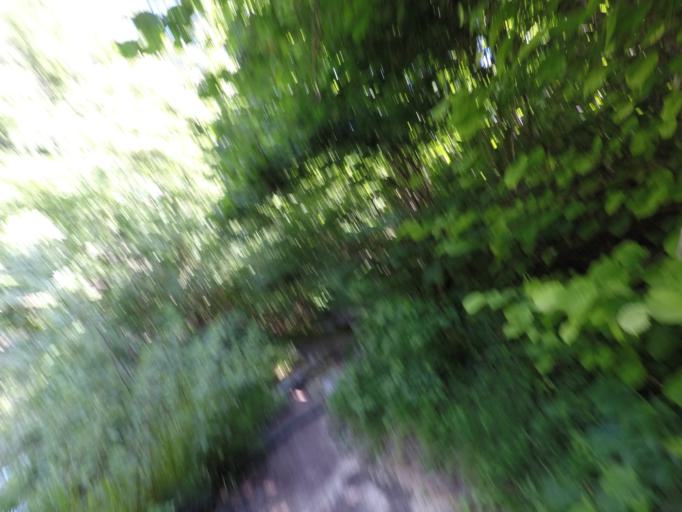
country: AZ
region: Qakh Rayon
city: Cinarli
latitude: 41.4927
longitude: 46.8587
